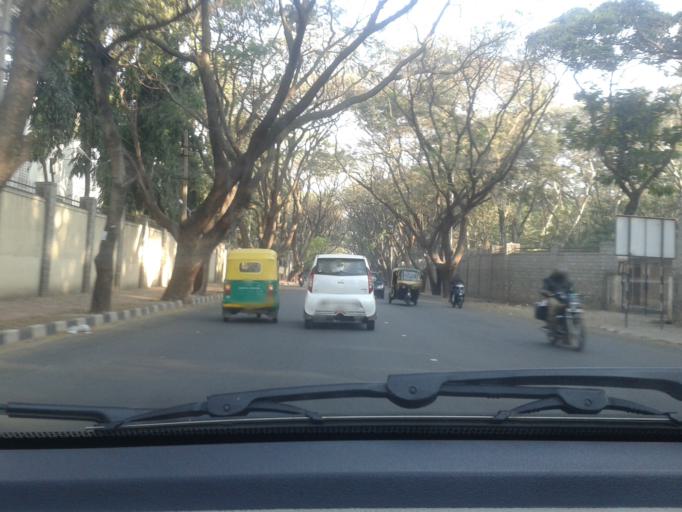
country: IN
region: Karnataka
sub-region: Bangalore Urban
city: Bangalore
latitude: 13.0240
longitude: 77.5721
